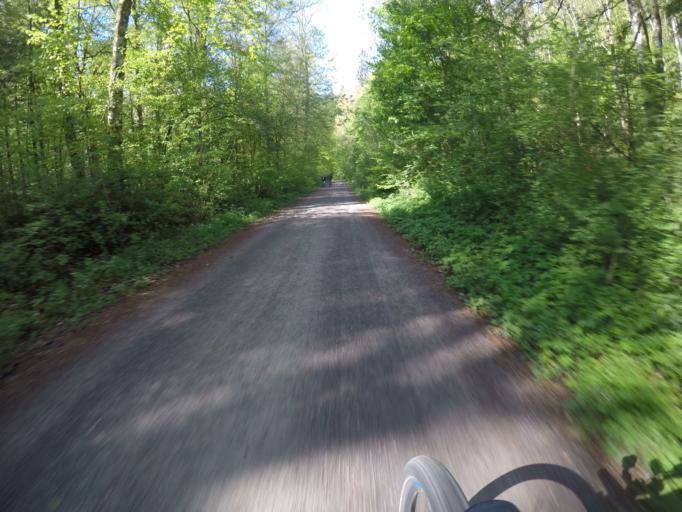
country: DE
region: Baden-Wuerttemberg
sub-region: Tuebingen Region
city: Tuebingen
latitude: 48.5521
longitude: 9.0772
